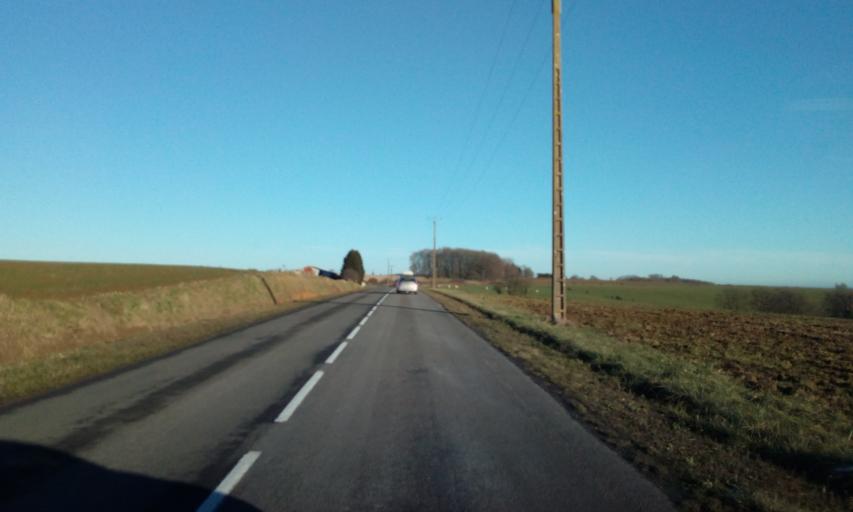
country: FR
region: Picardie
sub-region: Departement de l'Aisne
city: Rozoy-sur-Serre
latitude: 49.7145
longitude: 4.2358
